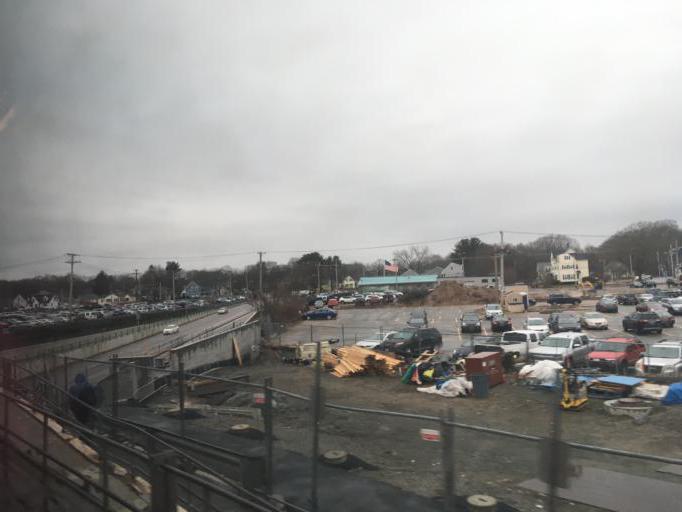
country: US
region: Massachusetts
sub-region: Bristol County
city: Mansfield
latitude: 42.0320
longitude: -71.2206
